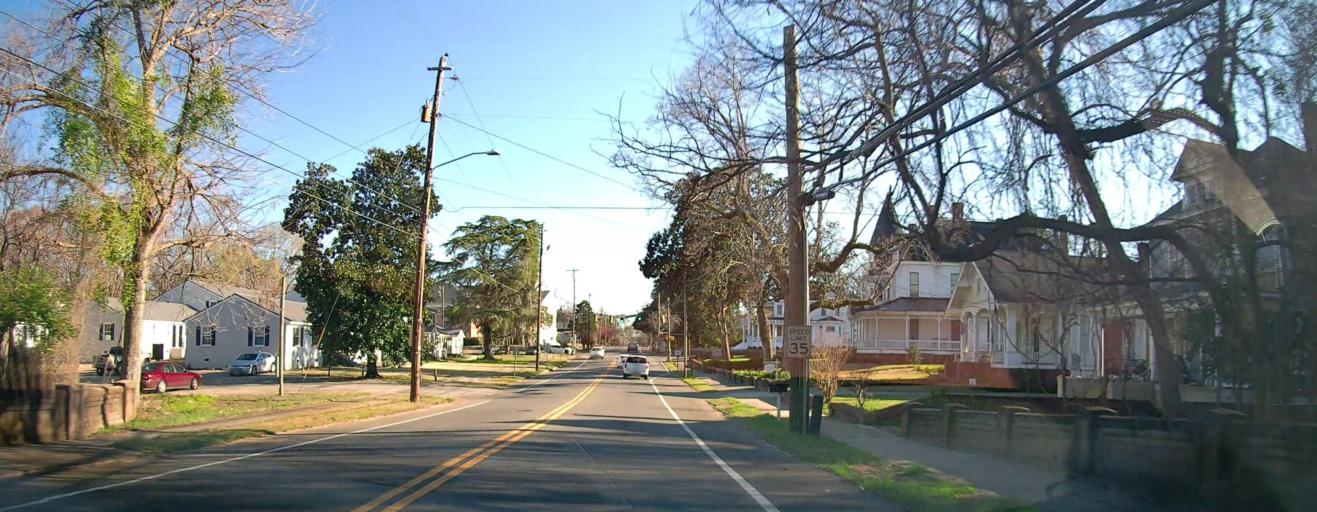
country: US
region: Georgia
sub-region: Sumter County
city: Americus
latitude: 32.0666
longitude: -84.2305
